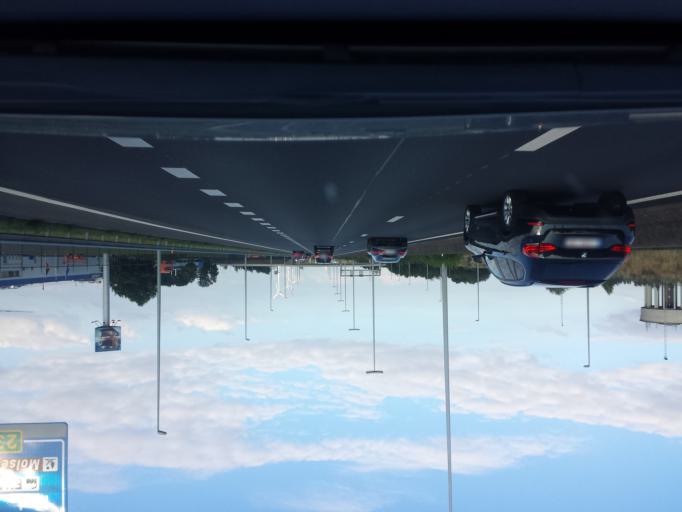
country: BE
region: Flanders
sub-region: Provincie Antwerpen
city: Westerlo
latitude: 51.1325
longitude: 4.9317
